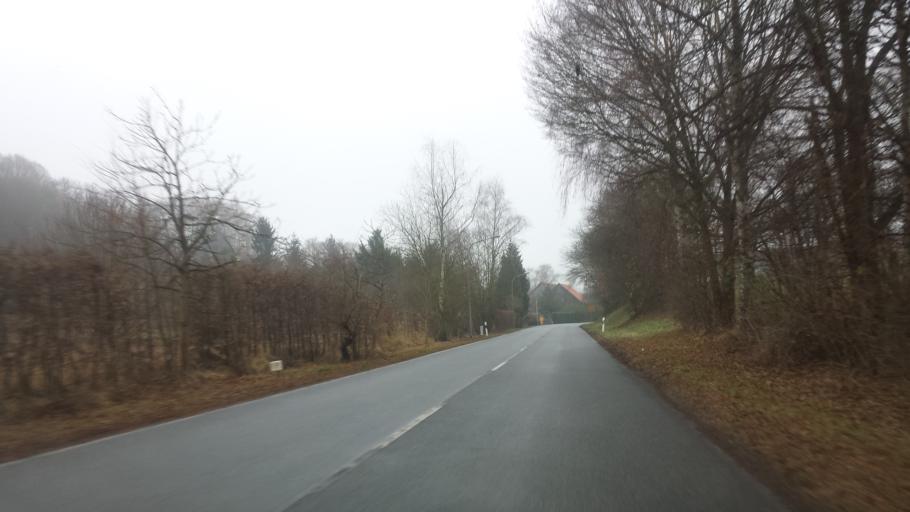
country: DE
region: Hesse
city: Ober-Ramstadt
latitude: 49.7784
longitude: 8.7153
